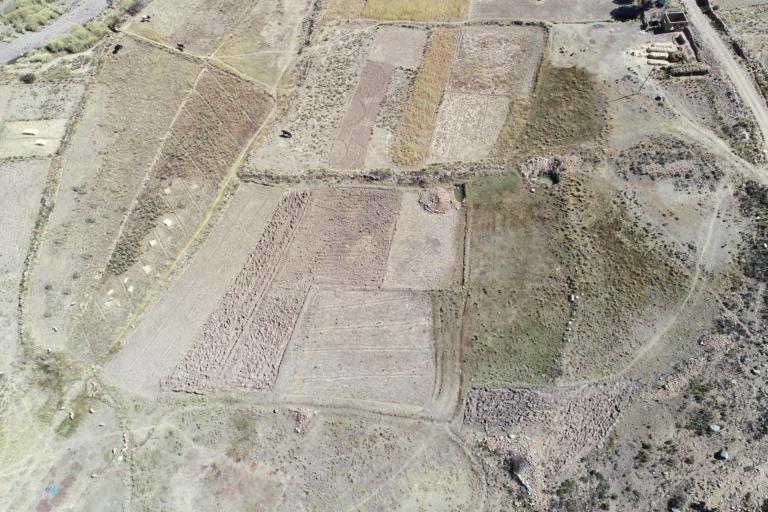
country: BO
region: La Paz
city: Achacachi
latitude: -15.8849
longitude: -68.8145
